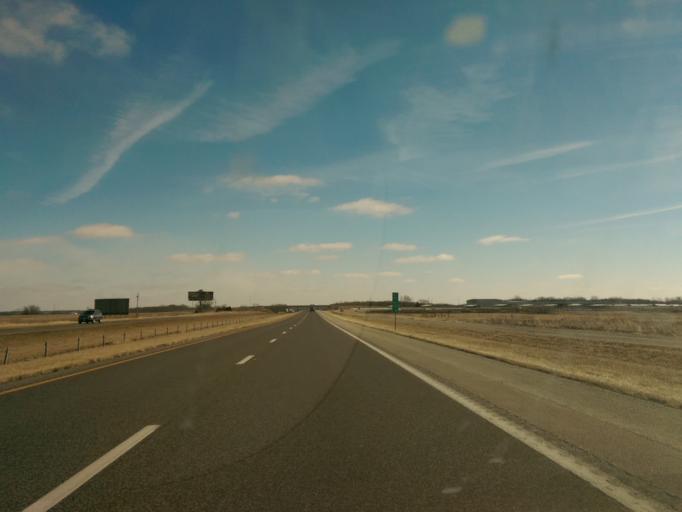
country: US
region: Missouri
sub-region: Callaway County
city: Fulton
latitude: 38.9414
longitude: -91.8726
